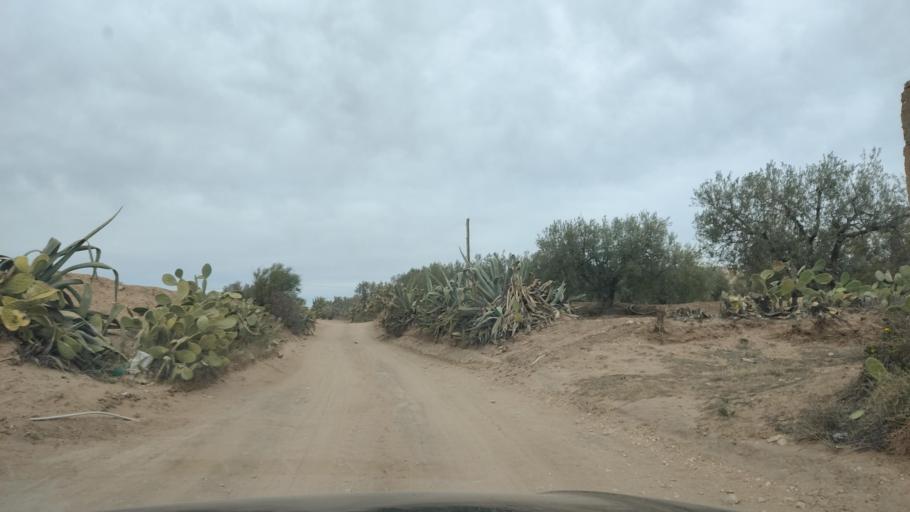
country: TN
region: Al Qasrayn
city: Kasserine
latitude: 35.2455
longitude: 8.9187
